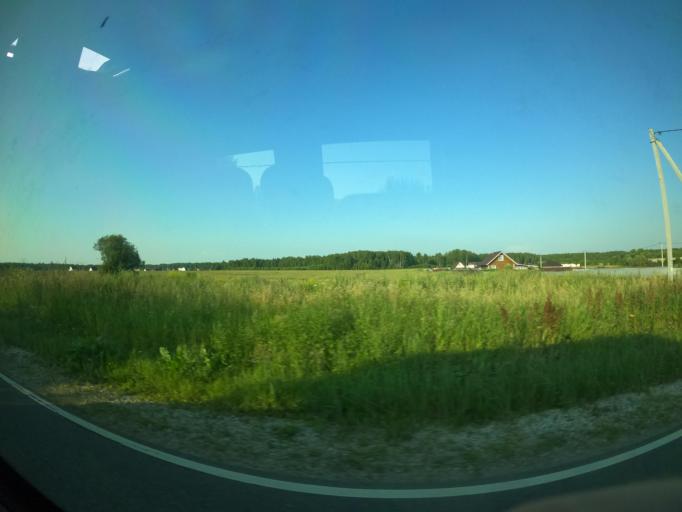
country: RU
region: Moskovskaya
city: Obolensk
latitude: 54.9372
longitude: 37.2461
